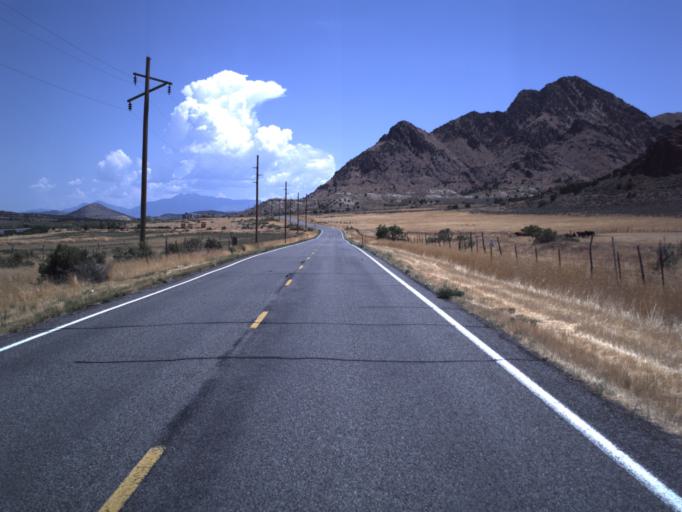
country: US
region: Utah
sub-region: Millard County
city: Delta
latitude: 39.5427
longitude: -112.2393
